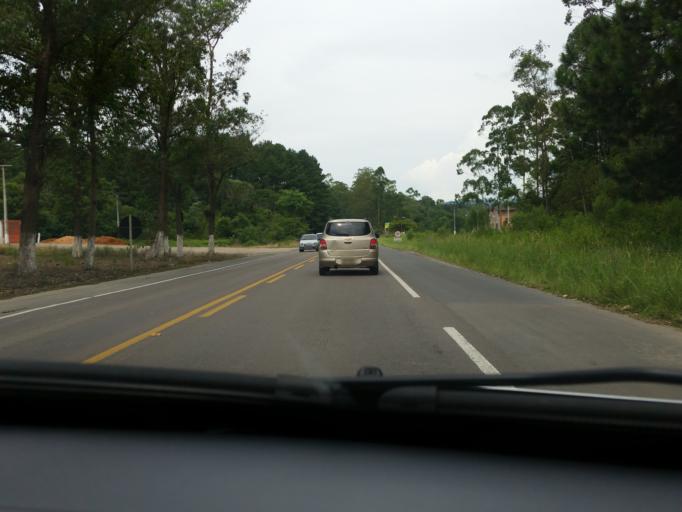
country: BR
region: Santa Catarina
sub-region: Rio Do Sul
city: Rio do Sul
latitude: -27.1718
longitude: -49.5801
